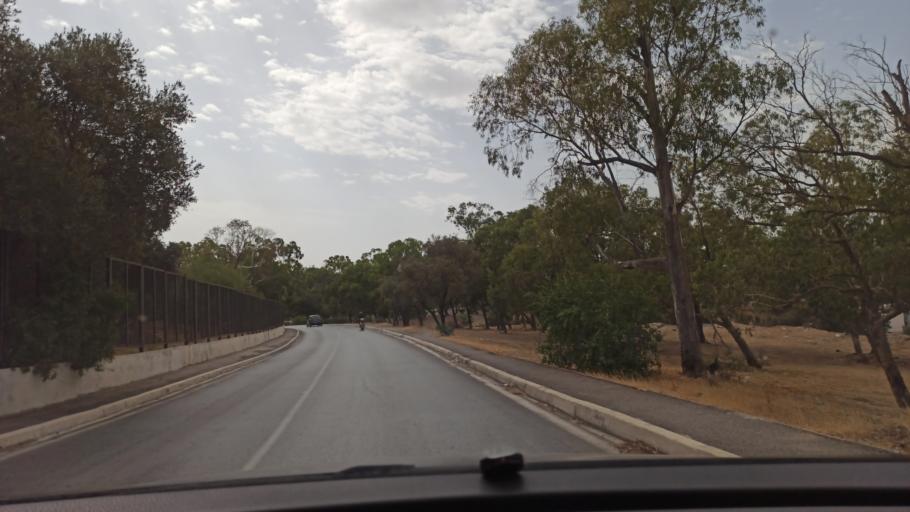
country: TN
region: Tunis
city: Tunis
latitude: 36.8266
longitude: 10.1677
